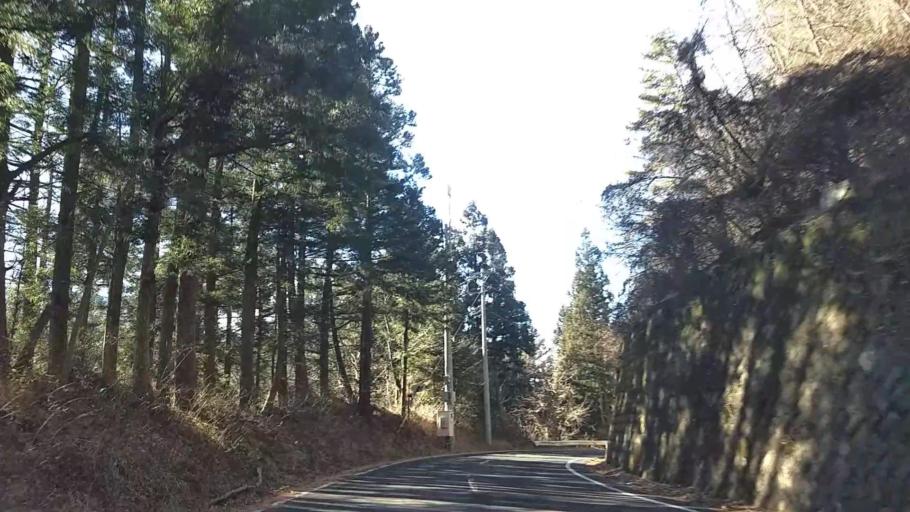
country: JP
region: Yamanashi
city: Otsuki
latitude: 35.5114
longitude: 138.9587
